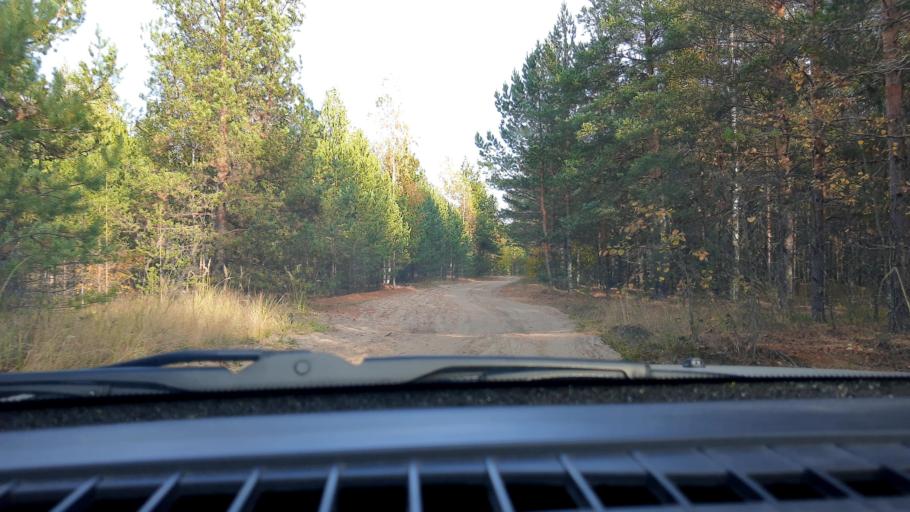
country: RU
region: Nizjnij Novgorod
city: Lukino
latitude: 56.3938
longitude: 43.6205
